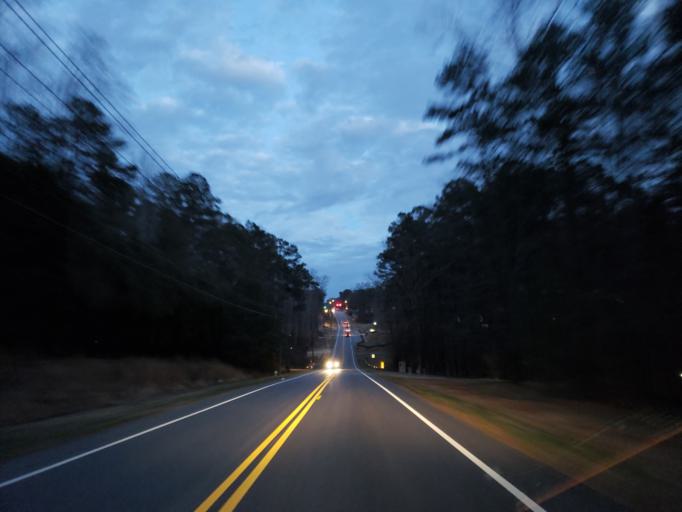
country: US
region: Georgia
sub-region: Cobb County
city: Kennesaw
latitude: 33.9990
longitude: -84.6631
